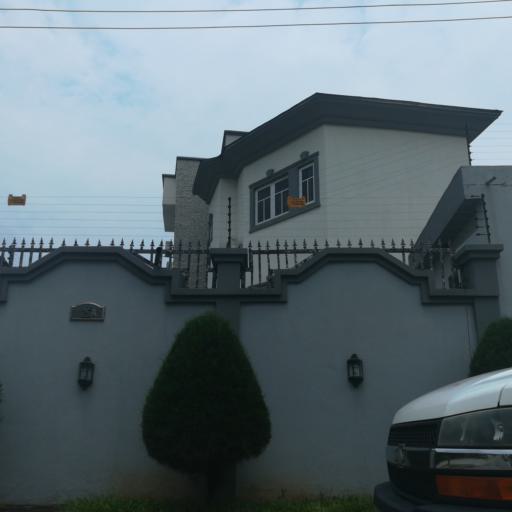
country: NG
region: Lagos
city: Ojota
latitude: 6.5749
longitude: 3.3831
